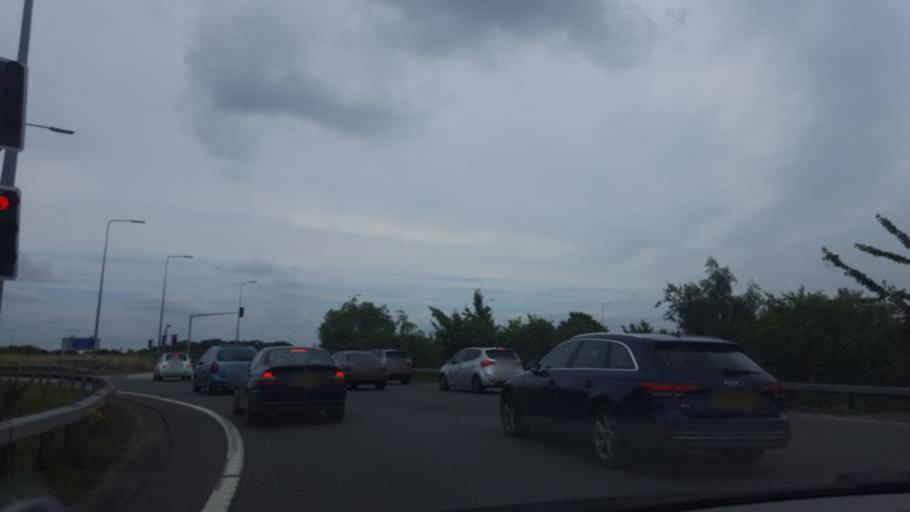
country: GB
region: England
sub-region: Royal Borough of Windsor and Maidenhead
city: Maidenhead
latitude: 51.4999
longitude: -0.7247
